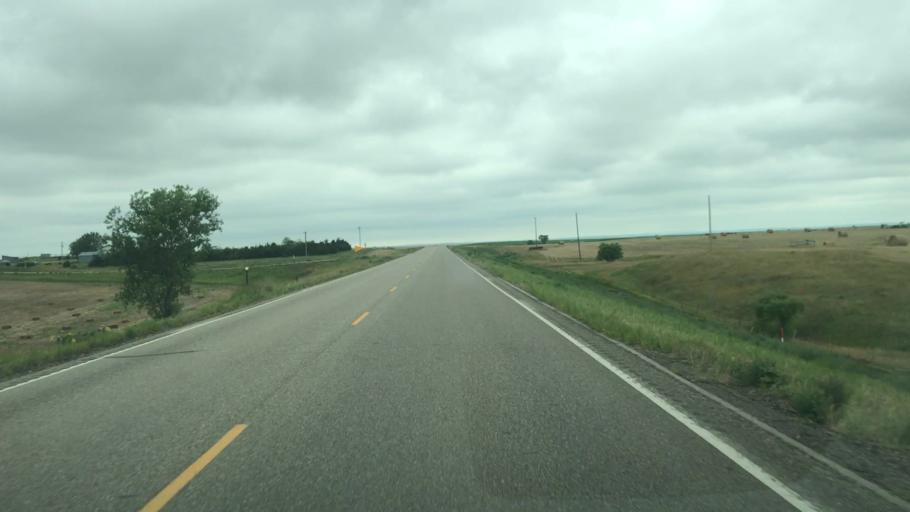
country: US
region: South Dakota
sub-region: Jackson County
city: Kadoka
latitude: 43.8228
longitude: -101.5224
